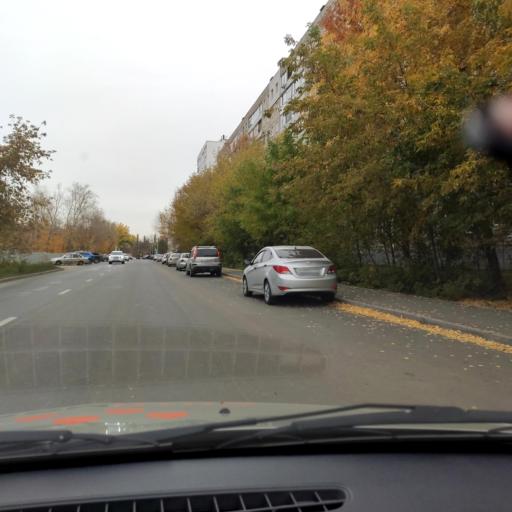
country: RU
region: Bashkortostan
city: Ufa
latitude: 54.7236
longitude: 56.0031
